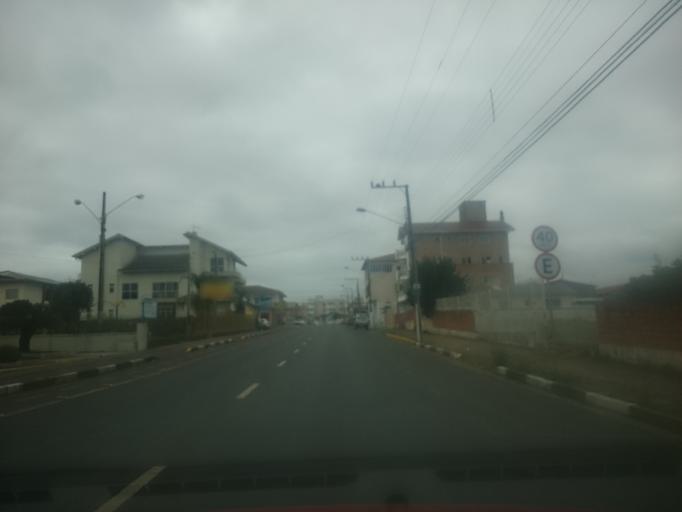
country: BR
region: Santa Catarina
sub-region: Lages
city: Lages
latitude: -27.8074
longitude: -50.3142
